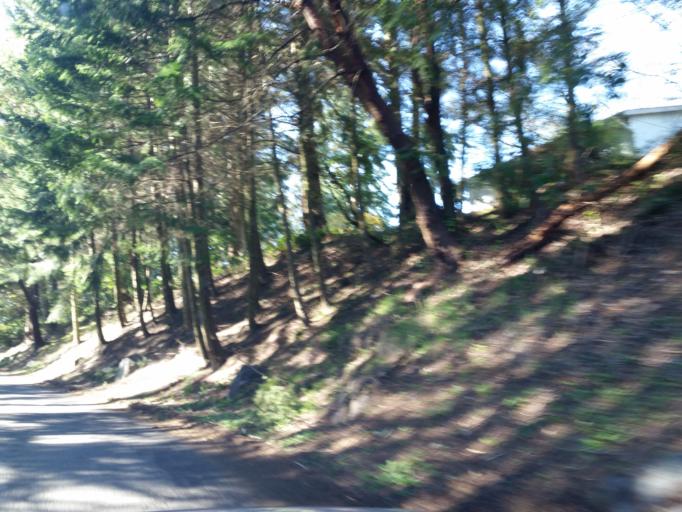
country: US
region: Washington
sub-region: Snohomish County
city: Esperance
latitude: 47.7886
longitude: -122.3677
